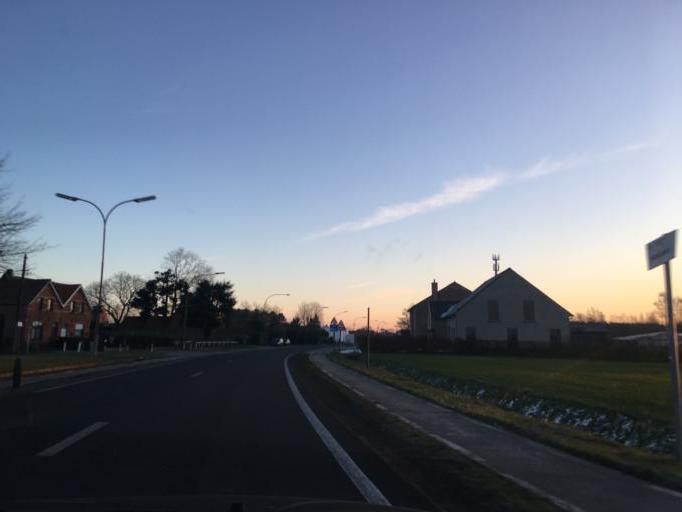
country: BE
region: Flanders
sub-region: Provincie Oost-Vlaanderen
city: Aalter
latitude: 51.1253
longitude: 3.4746
